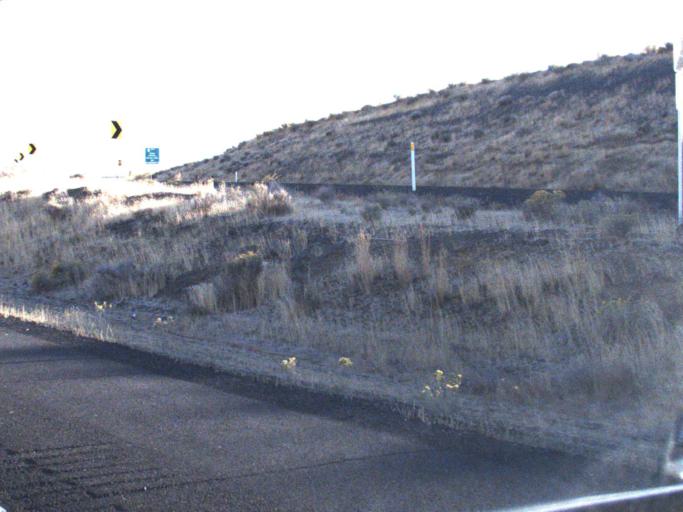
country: US
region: Washington
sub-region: Franklin County
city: Basin City
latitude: 46.5643
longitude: -118.9941
